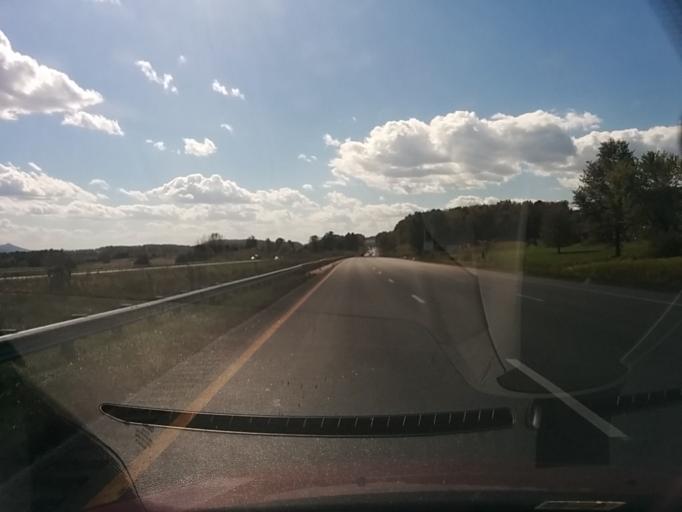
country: US
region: Virginia
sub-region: Augusta County
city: Stuarts Draft
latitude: 37.9292
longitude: -79.2330
